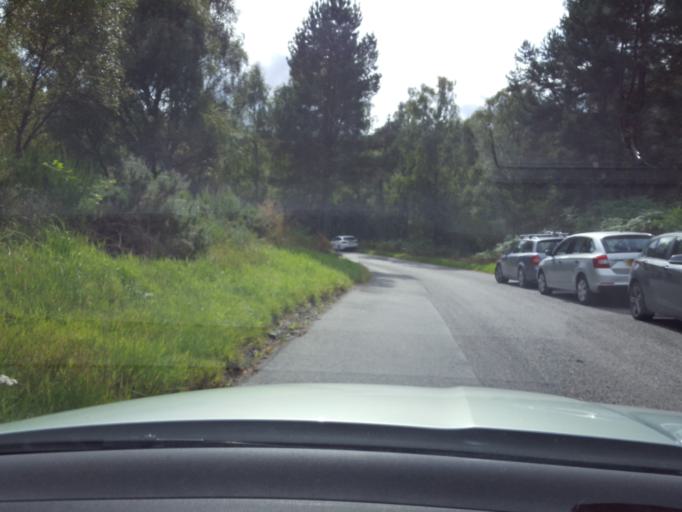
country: GB
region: Scotland
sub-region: Aberdeenshire
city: Ballater
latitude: 57.0845
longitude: -2.9431
